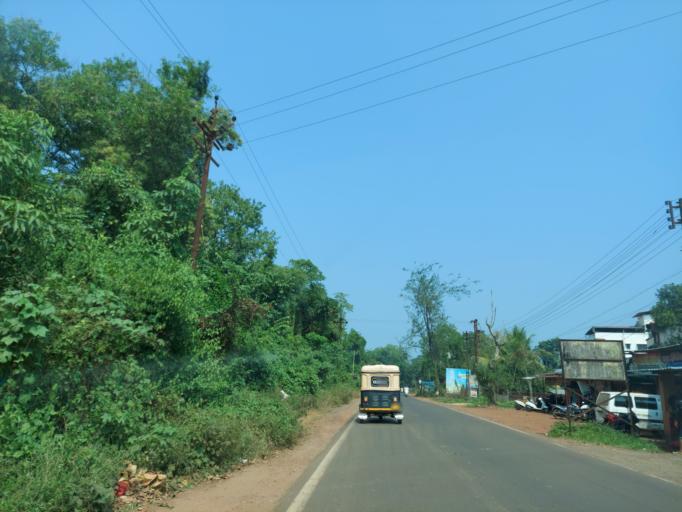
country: IN
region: Maharashtra
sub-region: Sindhudurg
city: Kudal
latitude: 15.9905
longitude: 73.6836
